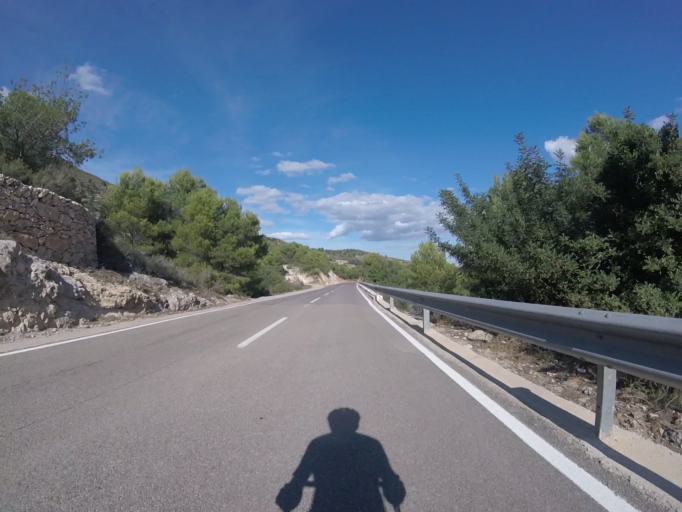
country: ES
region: Valencia
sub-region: Provincia de Castello
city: Alcala de Xivert
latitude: 40.3005
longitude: 0.1886
